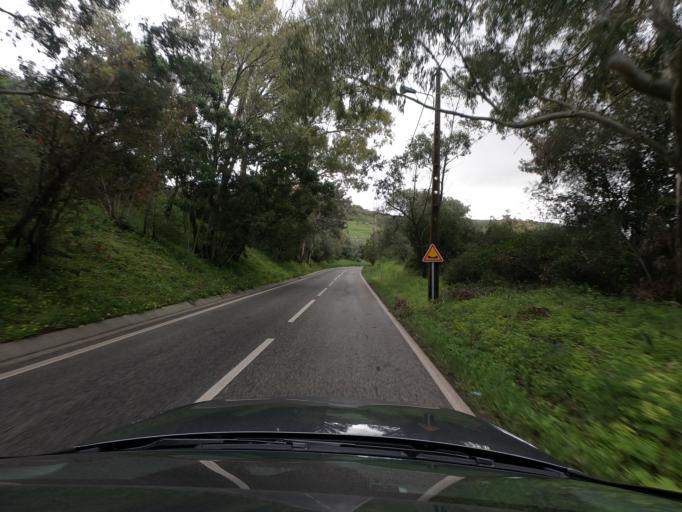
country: PT
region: Lisbon
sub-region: Oeiras
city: Quejas
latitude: 38.7396
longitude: -9.2623
